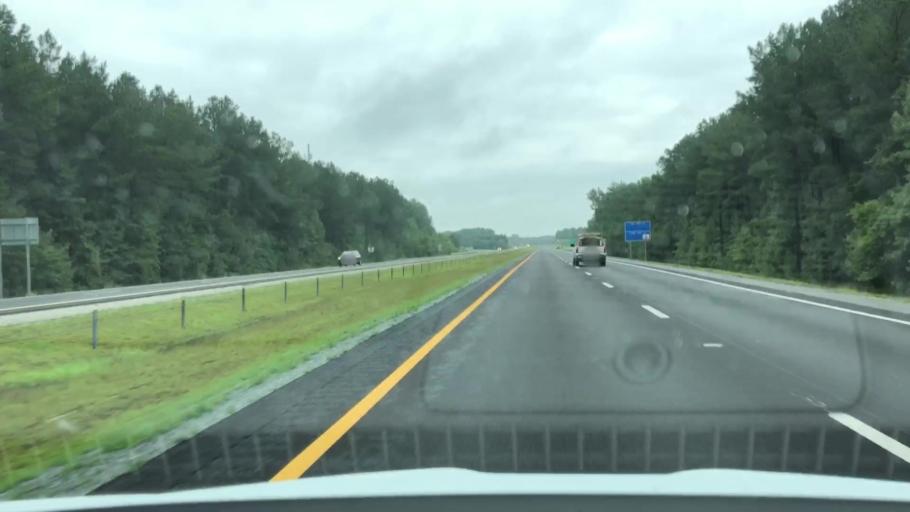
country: US
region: North Carolina
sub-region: Wayne County
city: Fremont
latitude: 35.4871
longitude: -77.9923
